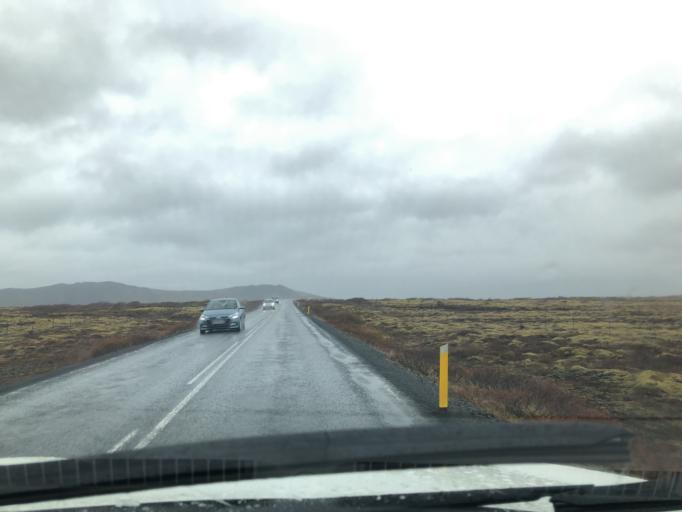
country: IS
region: South
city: Hveragerdi
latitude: 64.2026
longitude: -21.0362
